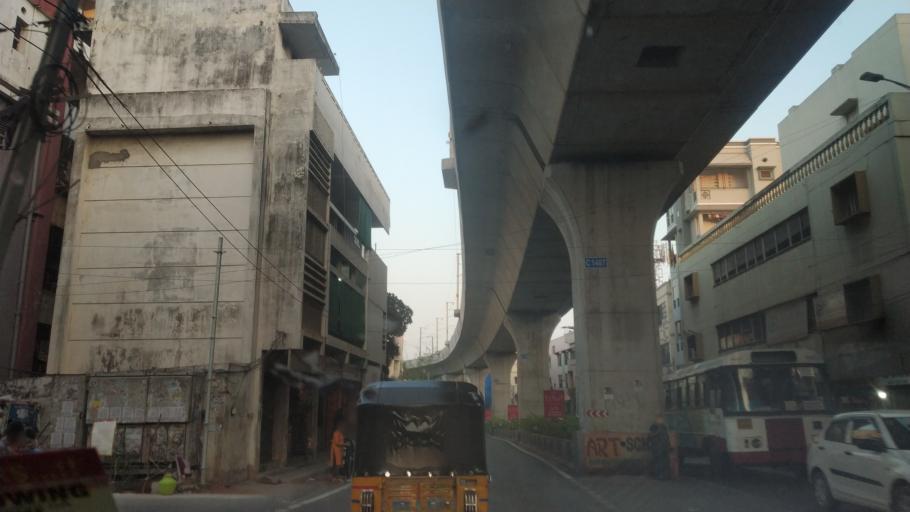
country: IN
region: Telangana
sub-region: Rangareddi
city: Kukatpalli
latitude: 17.4367
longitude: 78.4361
